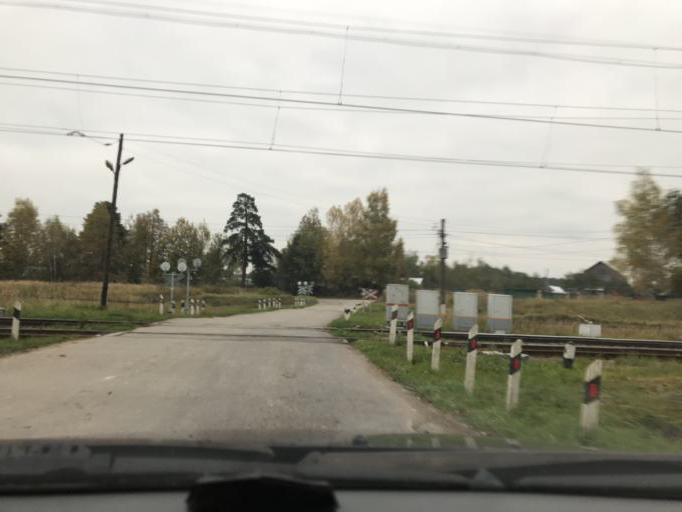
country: RU
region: Kaluga
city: Mstikhino
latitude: 54.6240
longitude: 36.1459
